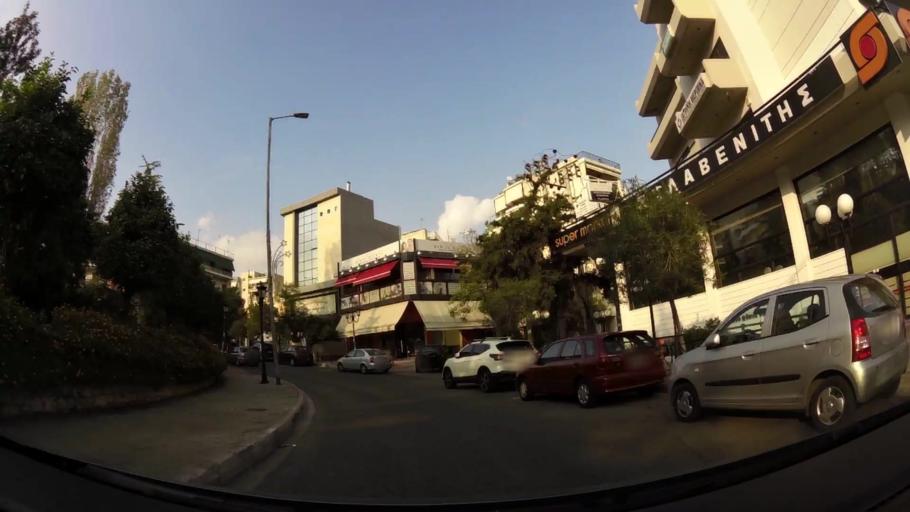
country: GR
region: Attica
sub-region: Nomarchia Athinas
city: Petroupolis
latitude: 38.0422
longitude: 23.6841
